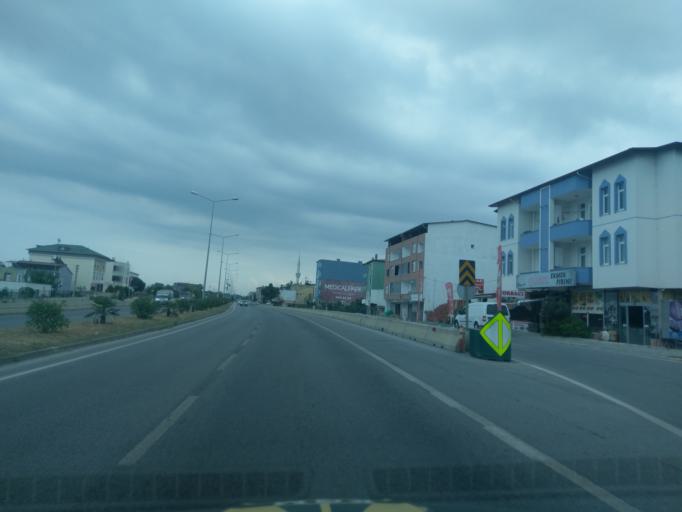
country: TR
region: Samsun
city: Taflan
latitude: 41.3882
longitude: 36.2048
